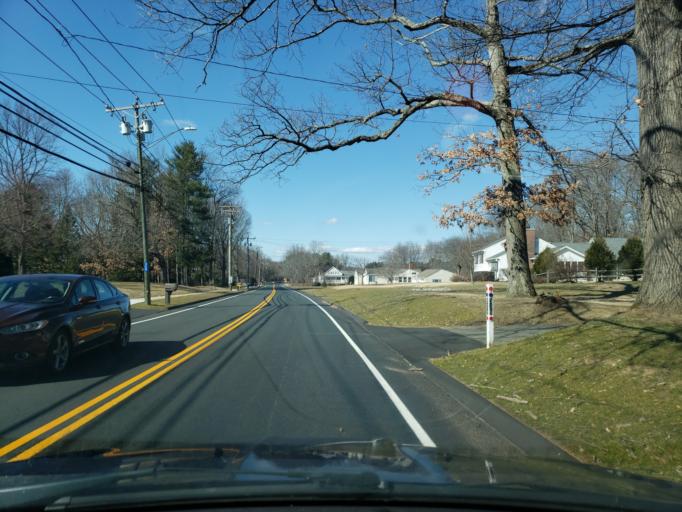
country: US
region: Connecticut
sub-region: Hartford County
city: Hazardville
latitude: 41.9930
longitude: -72.5513
